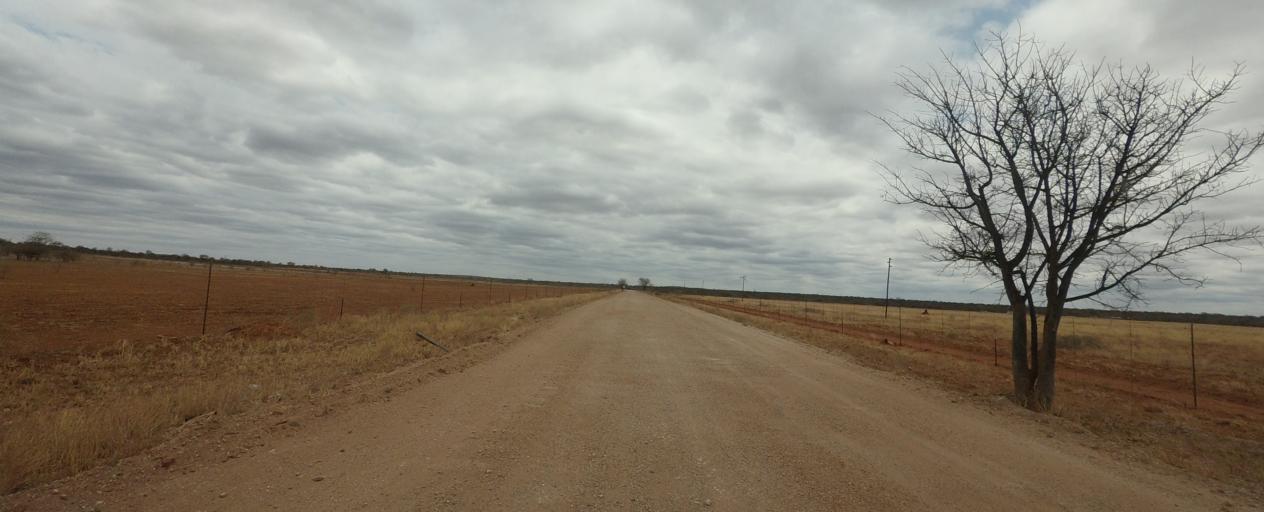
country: BW
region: Central
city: Mathathane
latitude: -22.7103
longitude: 28.5718
